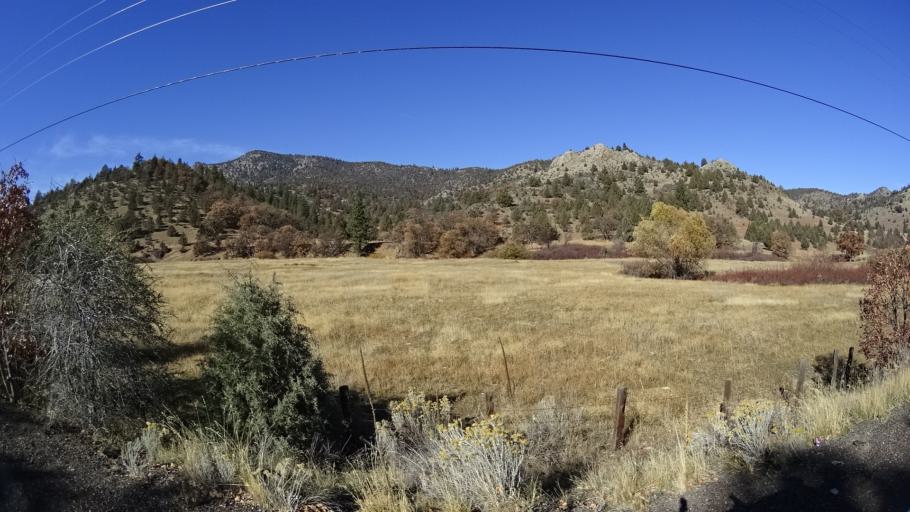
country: US
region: California
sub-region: Siskiyou County
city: Weed
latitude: 41.4703
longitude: -122.5913
